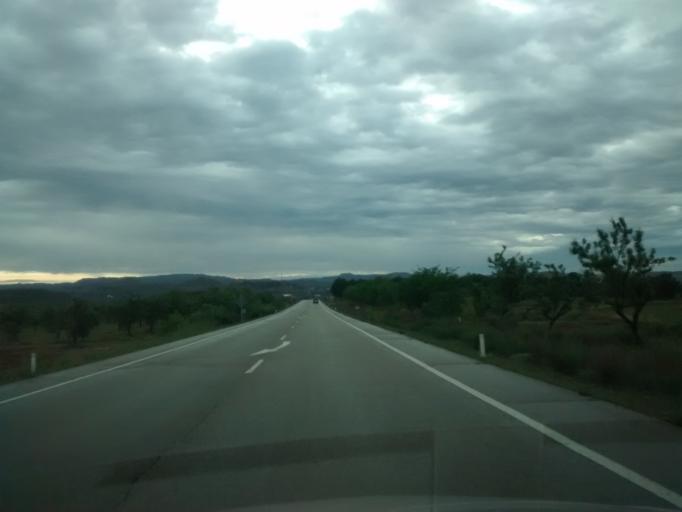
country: ES
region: Aragon
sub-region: Provincia de Zaragoza
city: Maella
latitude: 41.1130
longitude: 0.1552
